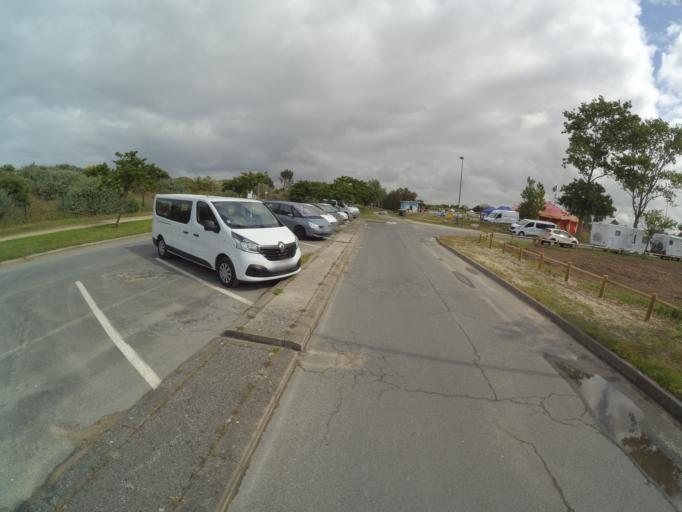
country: FR
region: Poitou-Charentes
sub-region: Departement de la Charente-Maritime
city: Angoulins
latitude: 46.1157
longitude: -1.1234
